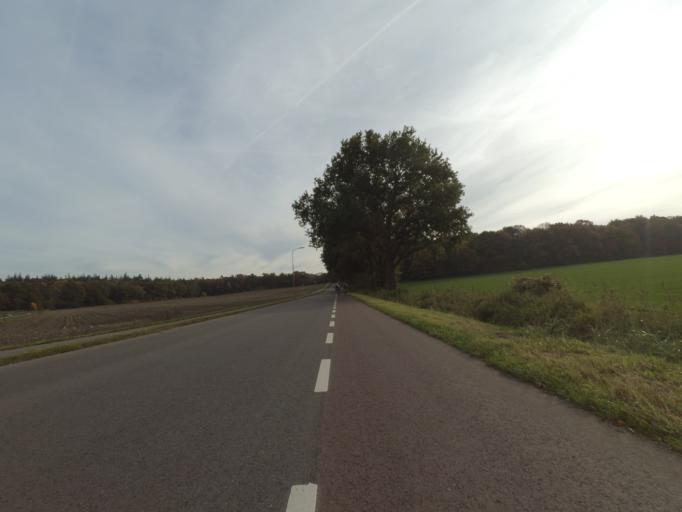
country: NL
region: Gelderland
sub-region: Gemeente Ede
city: Lunteren
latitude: 52.1022
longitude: 5.6396
